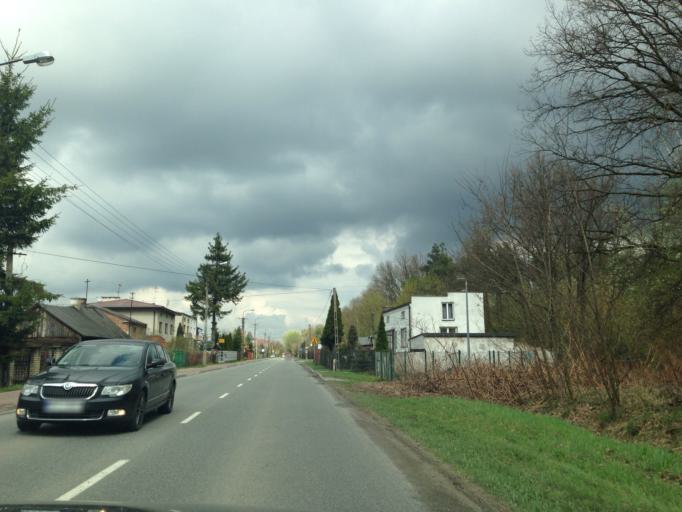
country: PL
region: Masovian Voivodeship
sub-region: Powiat warszawski zachodni
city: Babice
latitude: 52.2569
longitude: 20.8506
